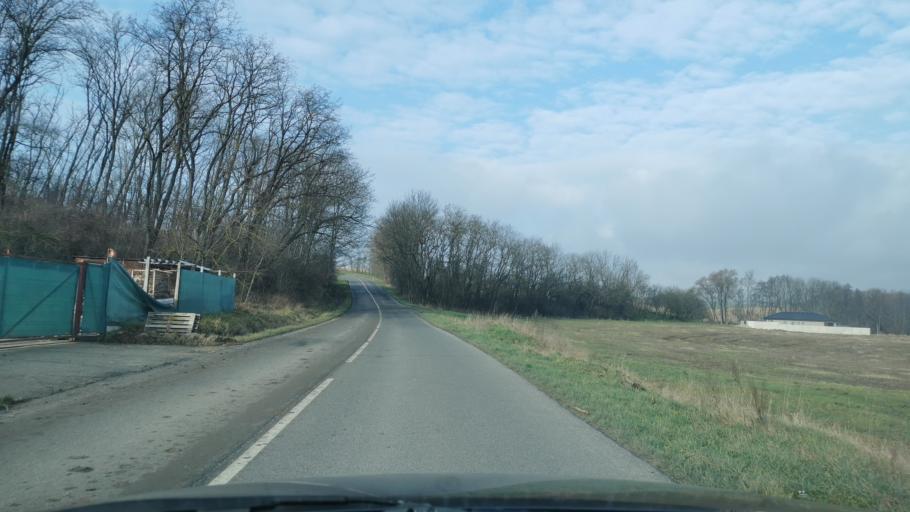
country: SK
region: Trnavsky
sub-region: Okres Senica
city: Senica
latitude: 48.7111
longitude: 17.3351
